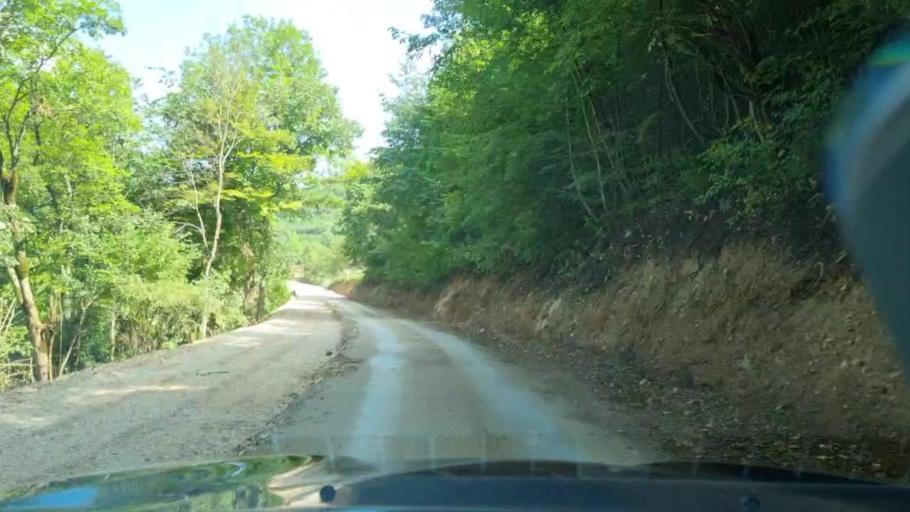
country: BA
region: Federation of Bosnia and Herzegovina
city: Kljuc
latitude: 44.5678
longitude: 16.8339
